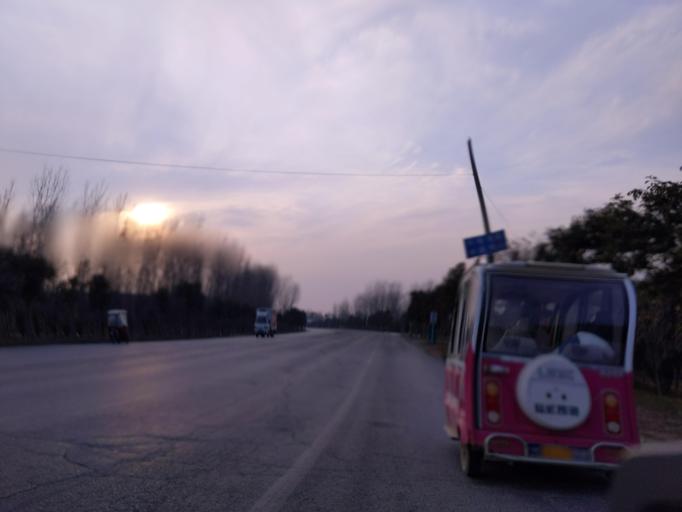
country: CN
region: Henan Sheng
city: Puyang
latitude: 35.8201
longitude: 114.9800
